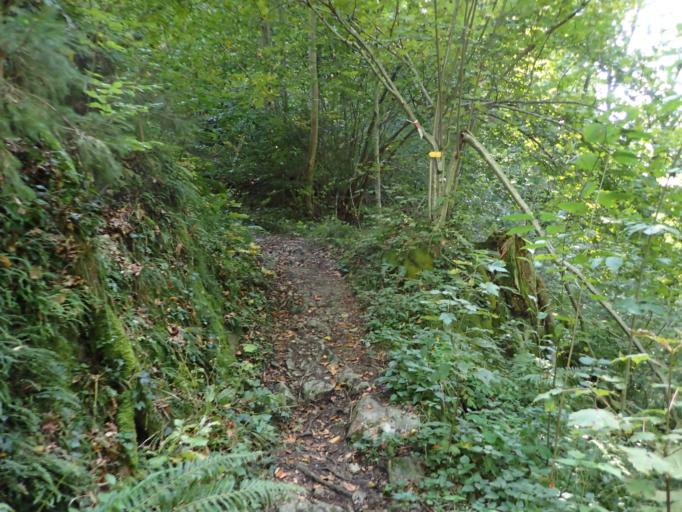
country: AT
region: Carinthia
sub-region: Politischer Bezirk Klagenfurt Land
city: Maria Worth
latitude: 46.6388
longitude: 14.1279
